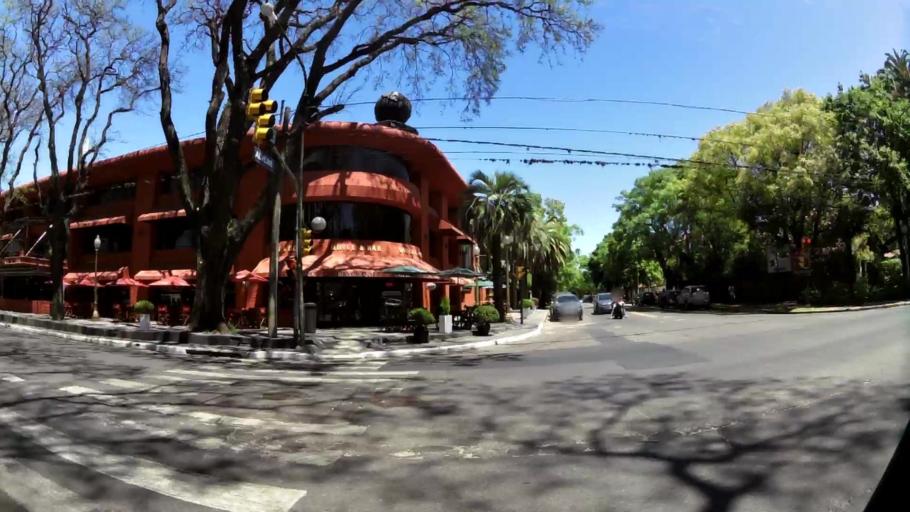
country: AR
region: Buenos Aires
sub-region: Partido de San Isidro
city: San Isidro
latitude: -34.4839
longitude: -58.4891
